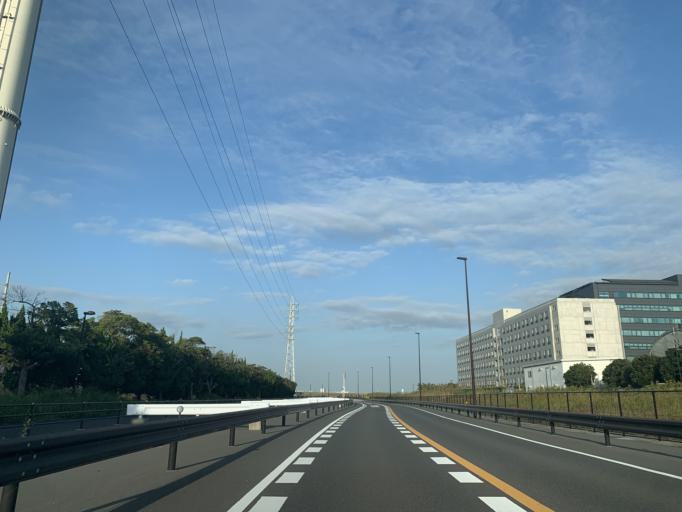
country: JP
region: Tokyo
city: Urayasu
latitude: 35.6501
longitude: 139.9218
